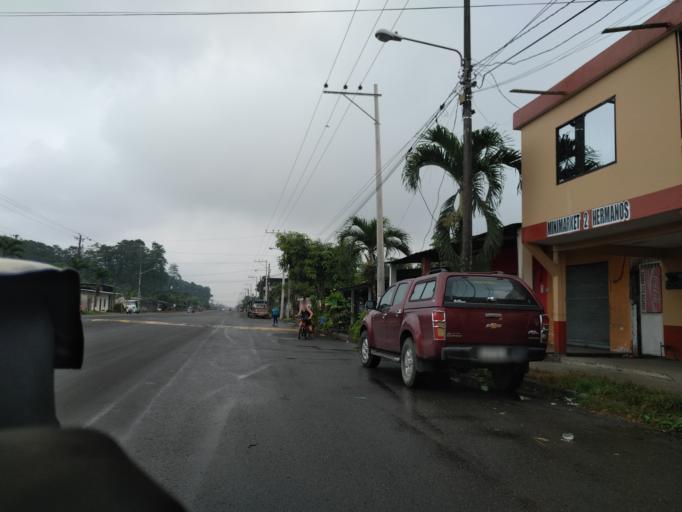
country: EC
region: Cotopaxi
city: La Mana
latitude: -0.9463
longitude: -79.3359
